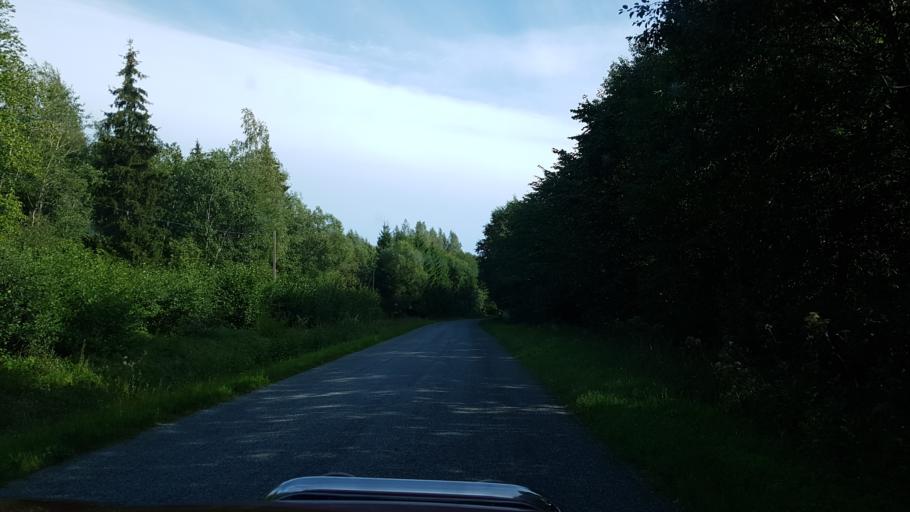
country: EE
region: Laeaene
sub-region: Lihula vald
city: Lihula
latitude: 58.4126
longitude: 24.0147
